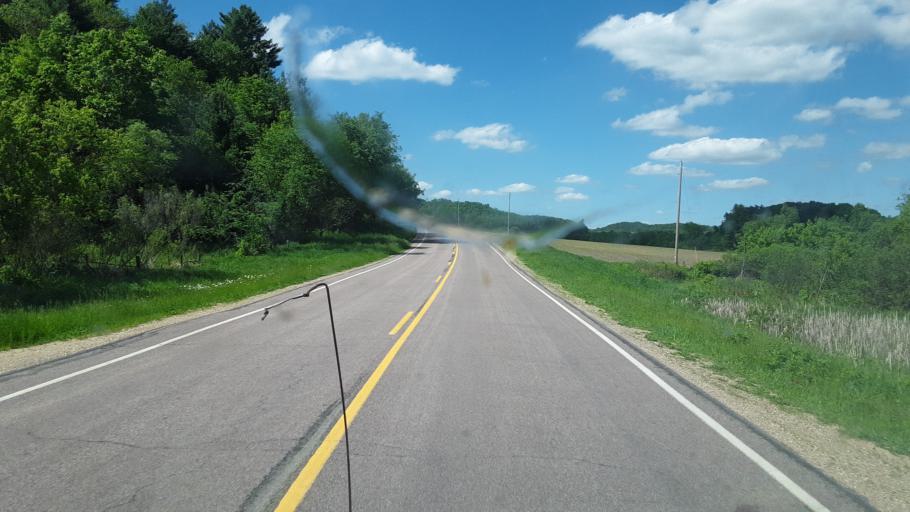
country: US
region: Wisconsin
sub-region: Richland County
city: Richland Center
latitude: 43.3951
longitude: -90.2417
